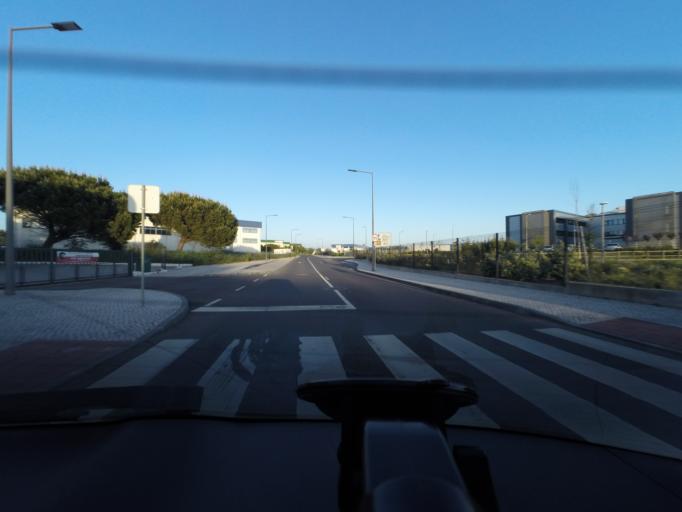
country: PT
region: Lisbon
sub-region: Cascais
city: Alcabideche
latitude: 38.7585
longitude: -9.3775
